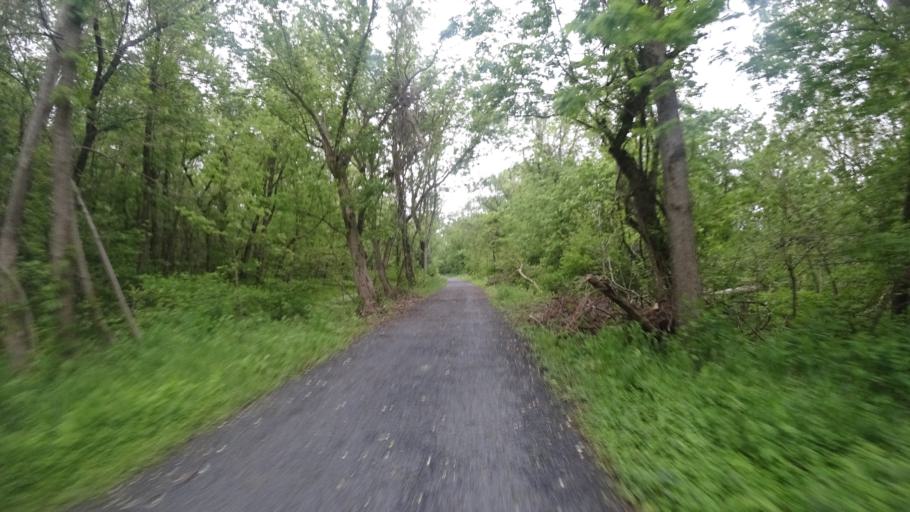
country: US
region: Maryland
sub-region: Frederick County
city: Brunswick
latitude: 39.3255
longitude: -77.6662
